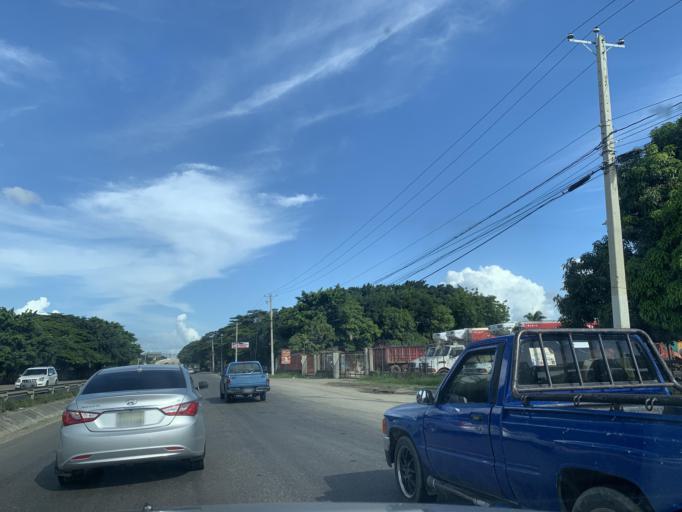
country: DO
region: Santiago
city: Villa Gonzalez
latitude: 19.5397
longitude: -70.7947
